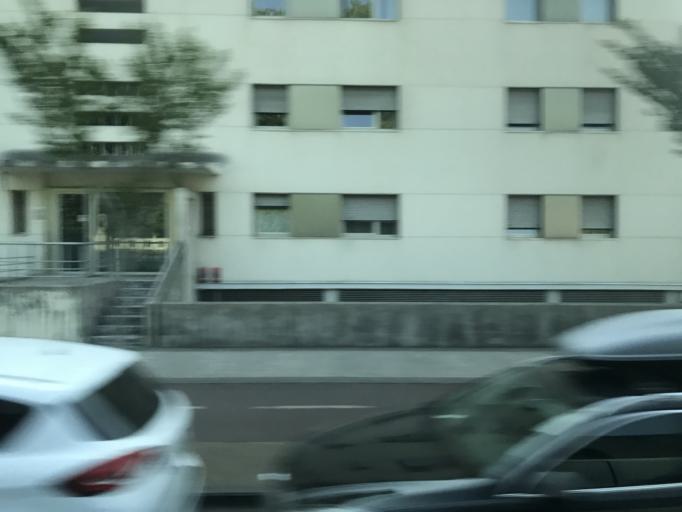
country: ES
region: Basque Country
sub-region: Provincia de Guipuzcoa
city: San Sebastian
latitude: 43.3141
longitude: -1.9776
